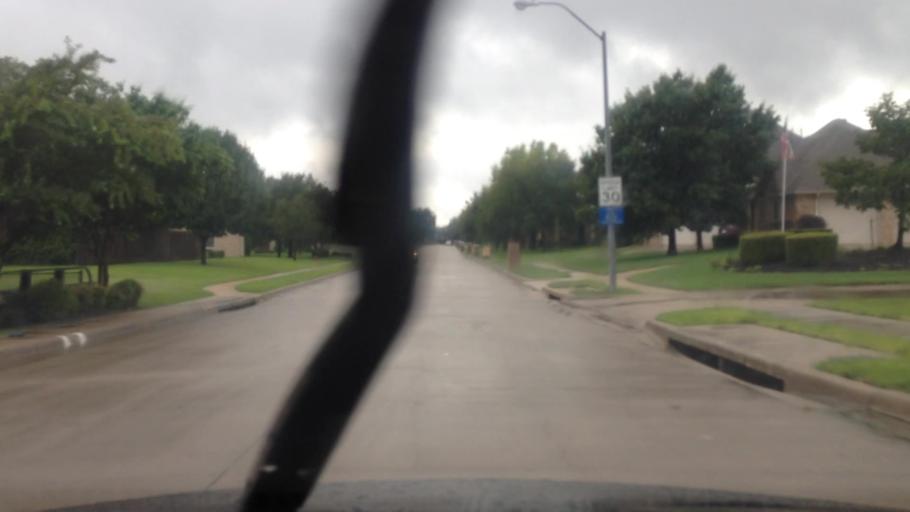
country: US
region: Texas
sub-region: Tarrant County
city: Colleyville
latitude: 32.9006
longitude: -97.1921
